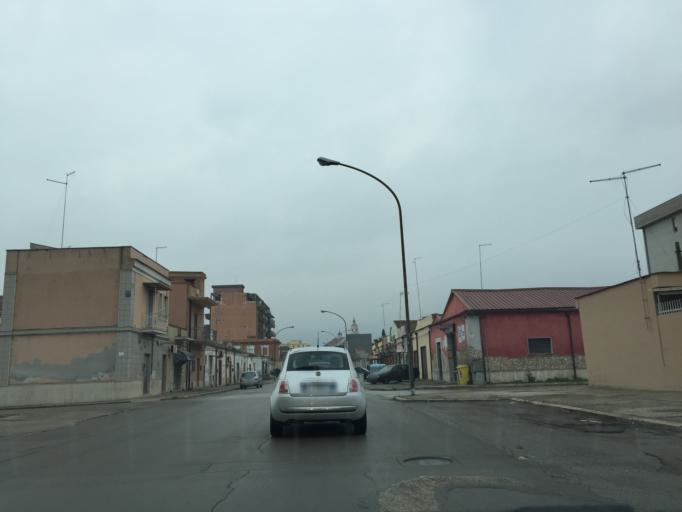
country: IT
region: Apulia
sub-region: Provincia di Foggia
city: Foggia
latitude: 41.4684
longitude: 15.5404
